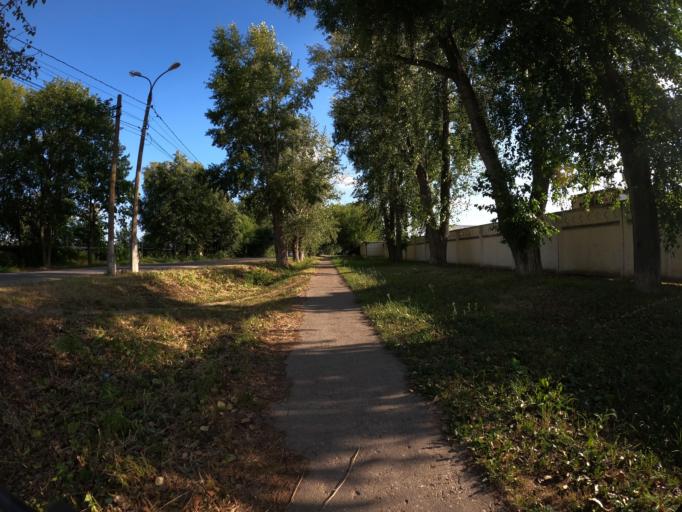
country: RU
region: Moskovskaya
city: Raduzhnyy
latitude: 55.1399
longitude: 38.7316
